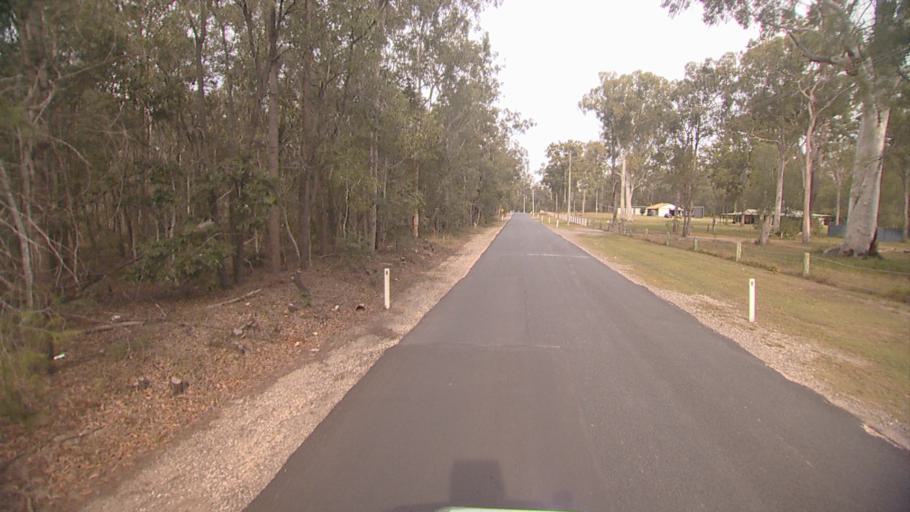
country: AU
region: Queensland
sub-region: Logan
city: Chambers Flat
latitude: -27.7803
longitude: 153.1180
